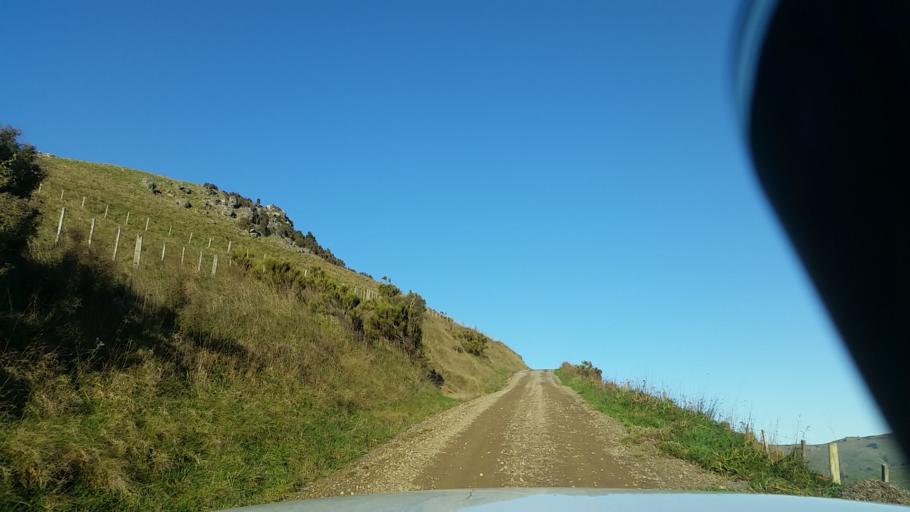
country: NZ
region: Canterbury
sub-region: Christchurch City
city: Christchurch
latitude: -43.7052
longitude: 173.0634
